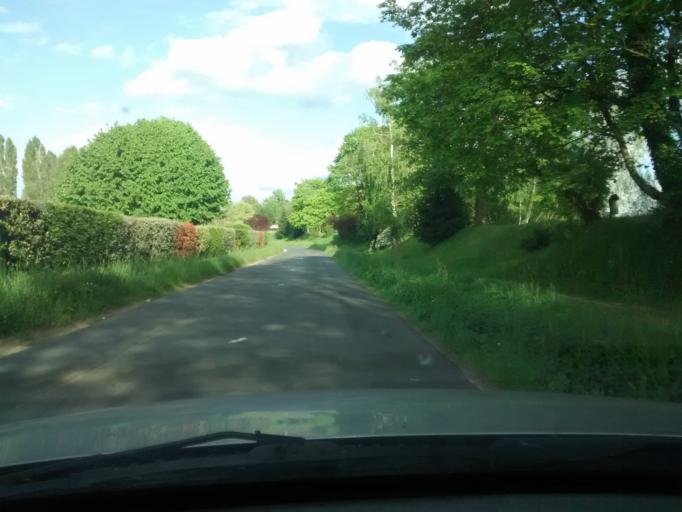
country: FR
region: Pays de la Loire
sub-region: Departement de la Sarthe
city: Brette-les-Pins
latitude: 47.9382
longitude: 0.3429
